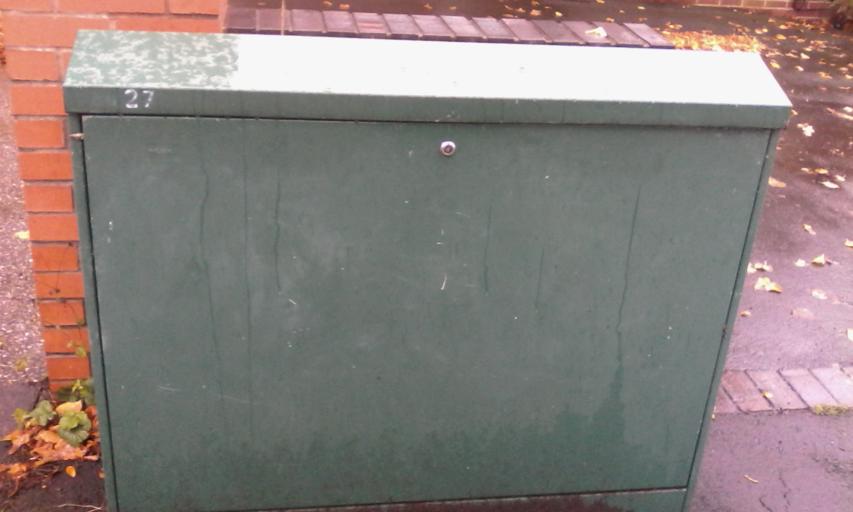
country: GB
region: England
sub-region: Nottinghamshire
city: Arnold
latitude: 52.9836
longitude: -1.1152
